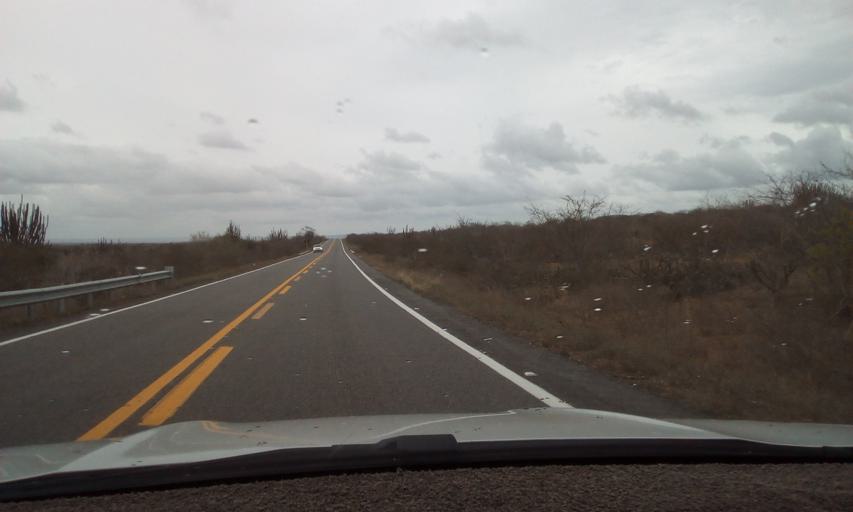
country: BR
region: Paraiba
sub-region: Areia
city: Remigio
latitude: -6.8843
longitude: -35.9221
